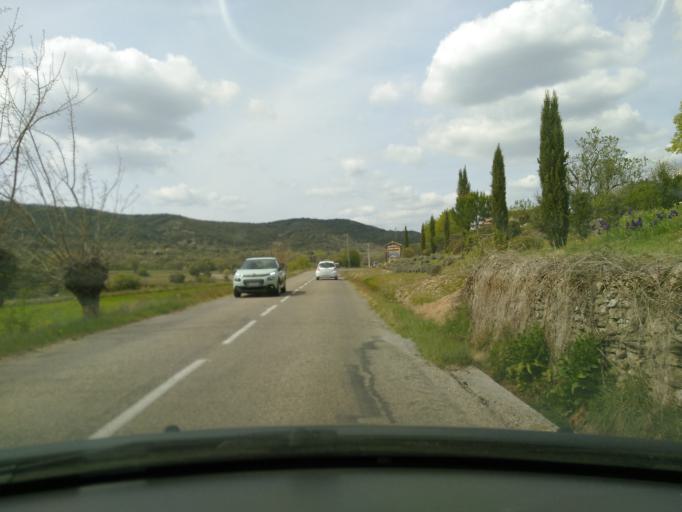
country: FR
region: Rhone-Alpes
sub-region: Departement de l'Ardeche
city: Ruoms
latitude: 44.4332
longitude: 4.4115
